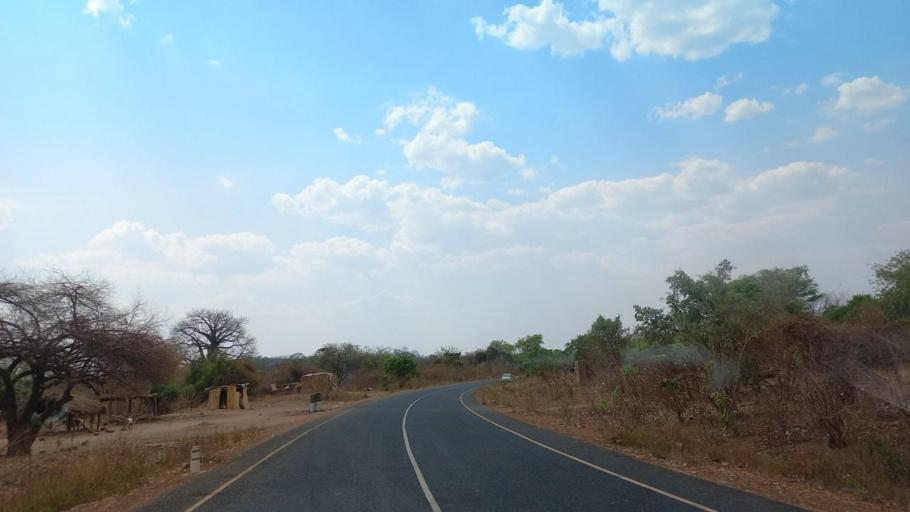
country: ZM
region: Lusaka
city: Luangwa
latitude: -15.3370
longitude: 30.3546
